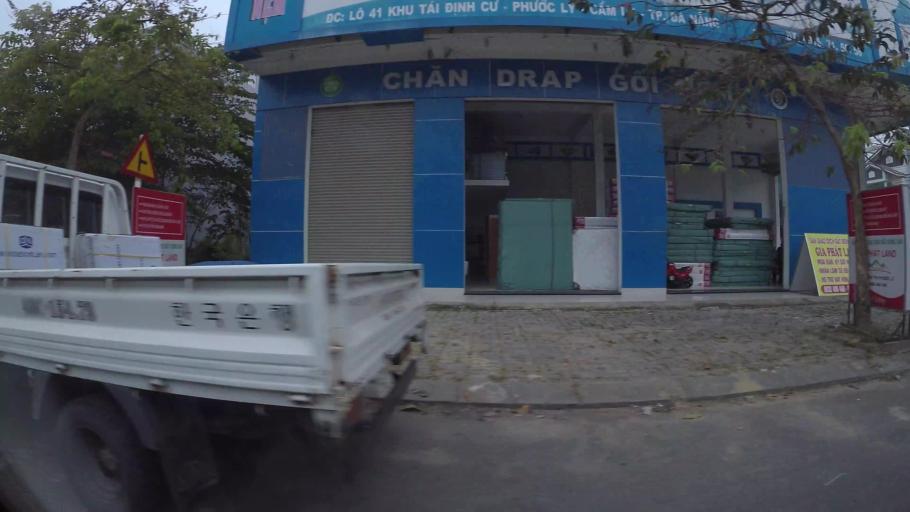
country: VN
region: Da Nang
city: Thanh Khe
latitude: 16.0445
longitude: 108.1788
